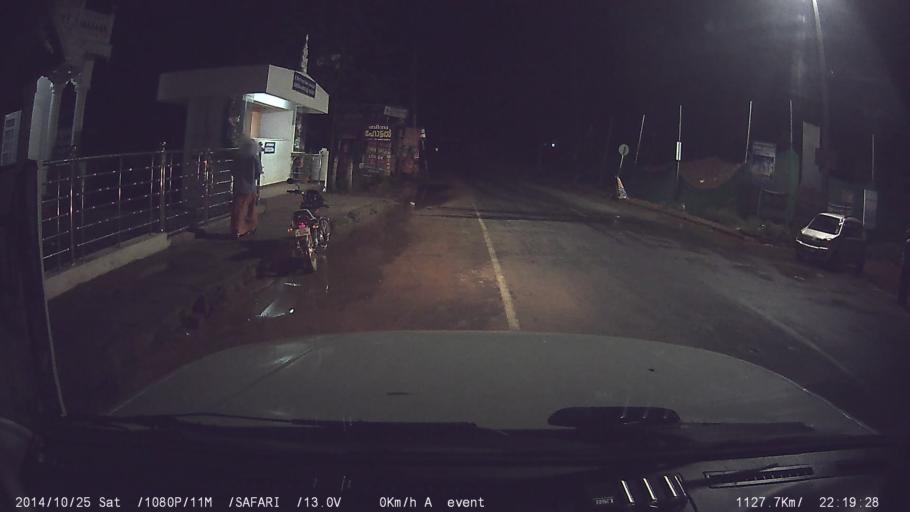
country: IN
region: Kerala
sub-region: Kottayam
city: Palackattumala
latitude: 9.7539
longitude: 76.5615
